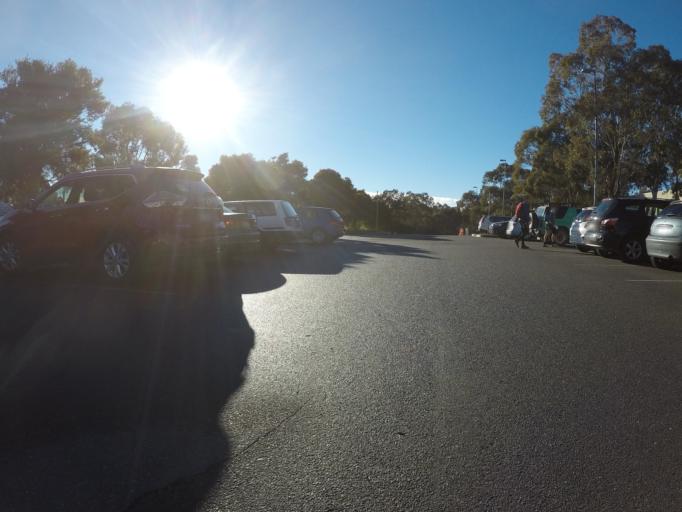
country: AU
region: Australian Capital Territory
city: Belconnen
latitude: -35.2401
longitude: 149.0877
